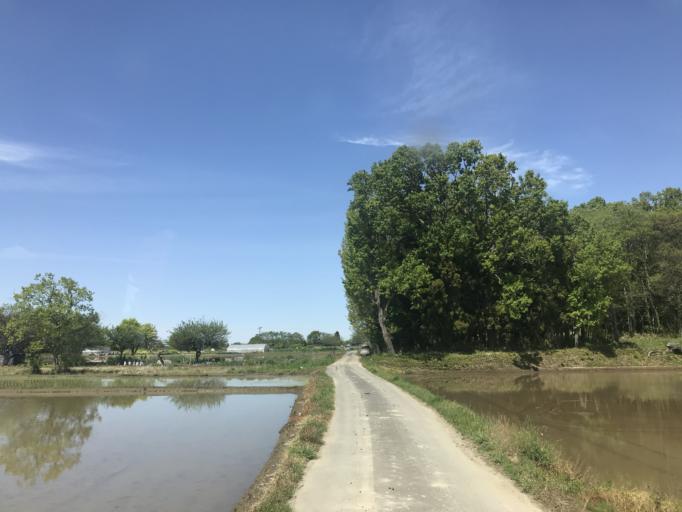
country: JP
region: Ibaraki
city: Mitsukaido
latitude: 36.0147
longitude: 139.9806
